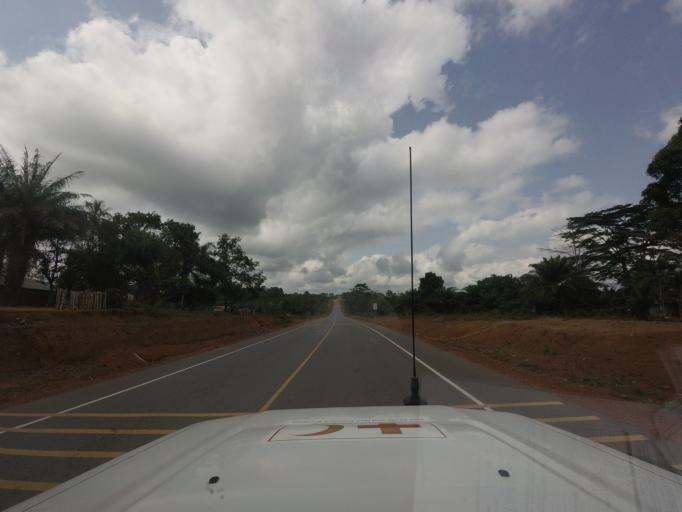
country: LR
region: Nimba
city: Sanniquellie
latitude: 7.2027
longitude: -9.0173
